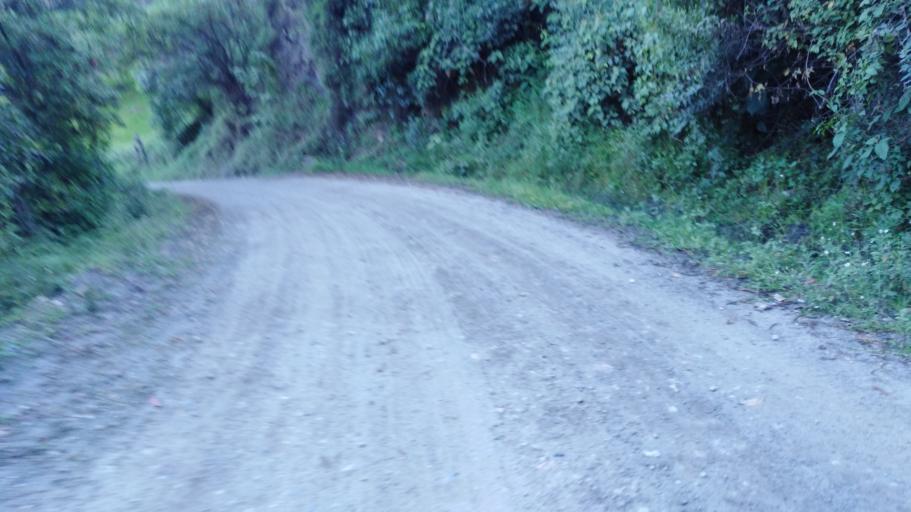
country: CO
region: Boyaca
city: San Mateo
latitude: 6.4026
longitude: -72.5651
